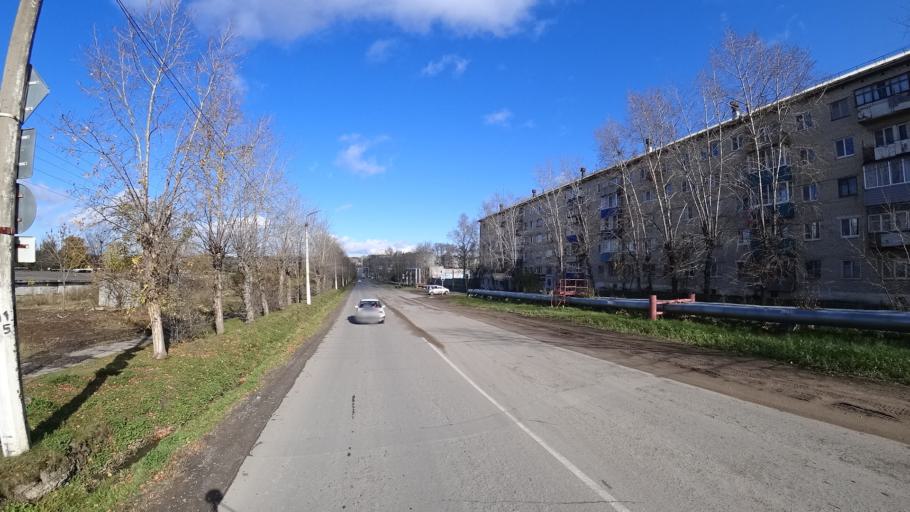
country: RU
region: Khabarovsk Krai
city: Amursk
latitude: 50.2234
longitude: 136.9014
